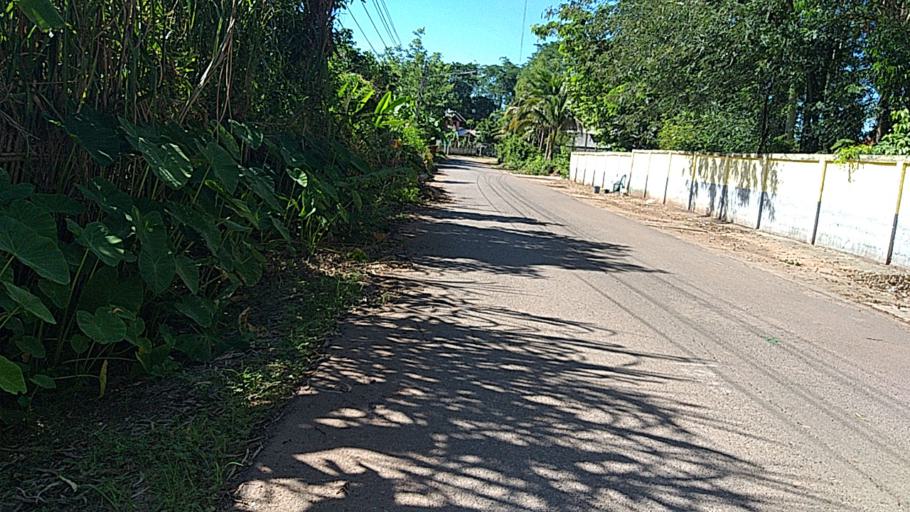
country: TH
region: Chaiyaphum
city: Ban Thaen
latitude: 16.4056
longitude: 102.3522
